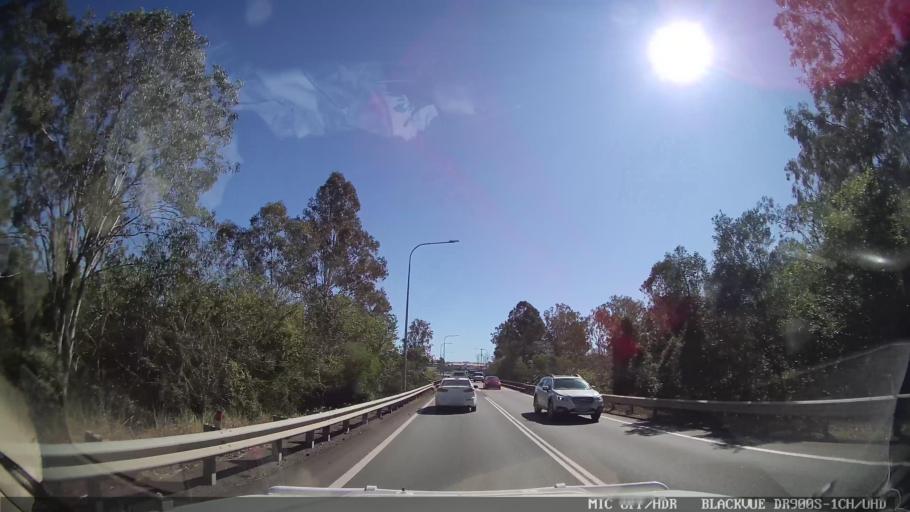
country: AU
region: Queensland
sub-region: Gympie Regional Council
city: Monkland
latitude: -26.2334
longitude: 152.6981
